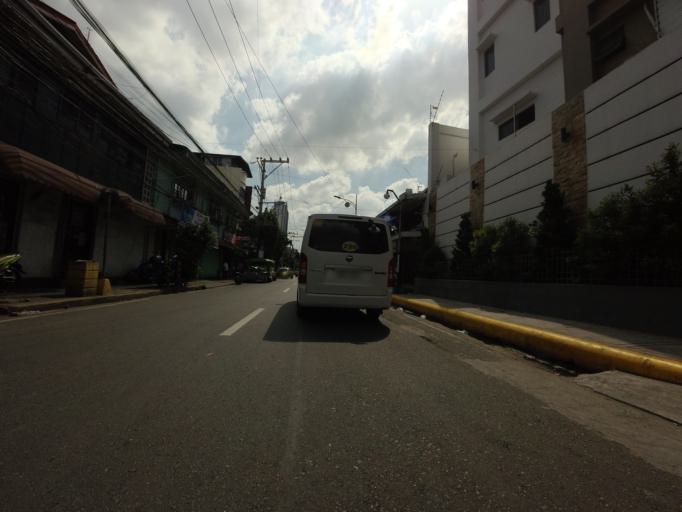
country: PH
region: Metro Manila
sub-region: City of Manila
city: Port Area
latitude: 14.5680
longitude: 120.9963
